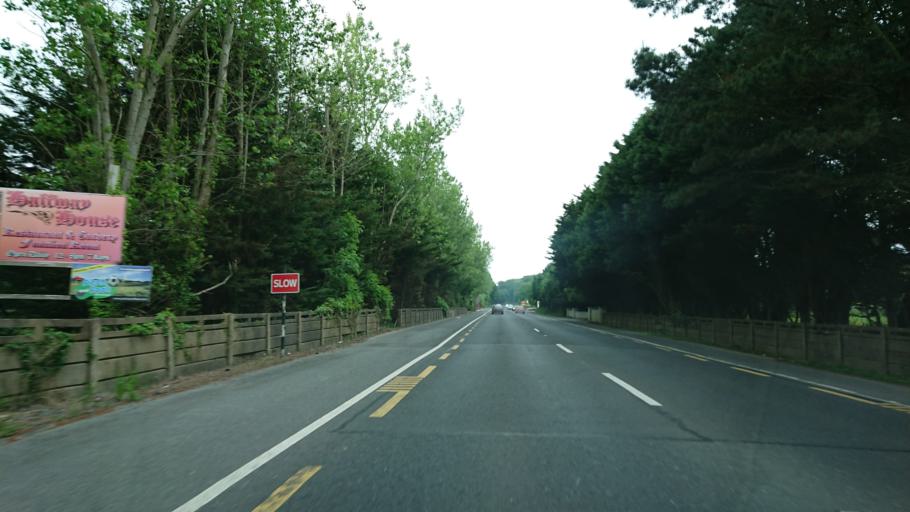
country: IE
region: Munster
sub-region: Waterford
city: Waterford
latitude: 52.2046
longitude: -7.1162
